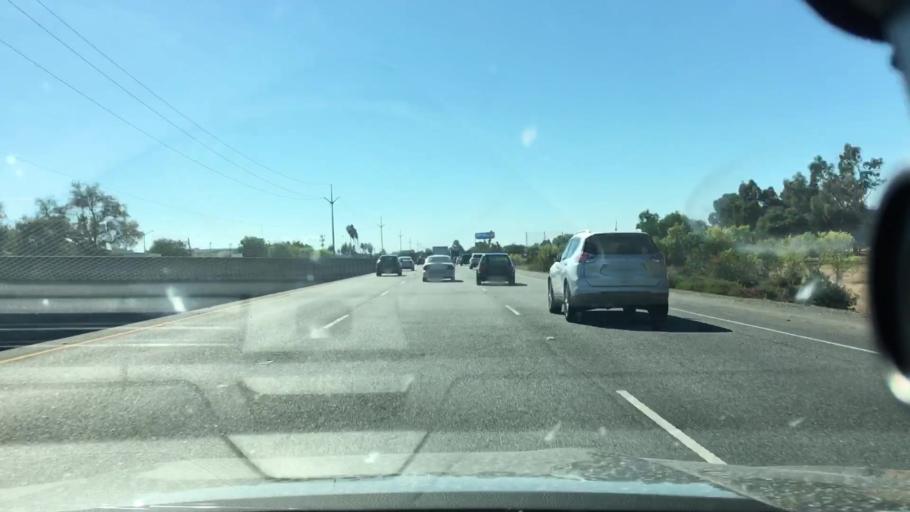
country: US
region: California
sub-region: Sacramento County
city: Arden-Arcade
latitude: 38.6344
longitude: -121.3911
